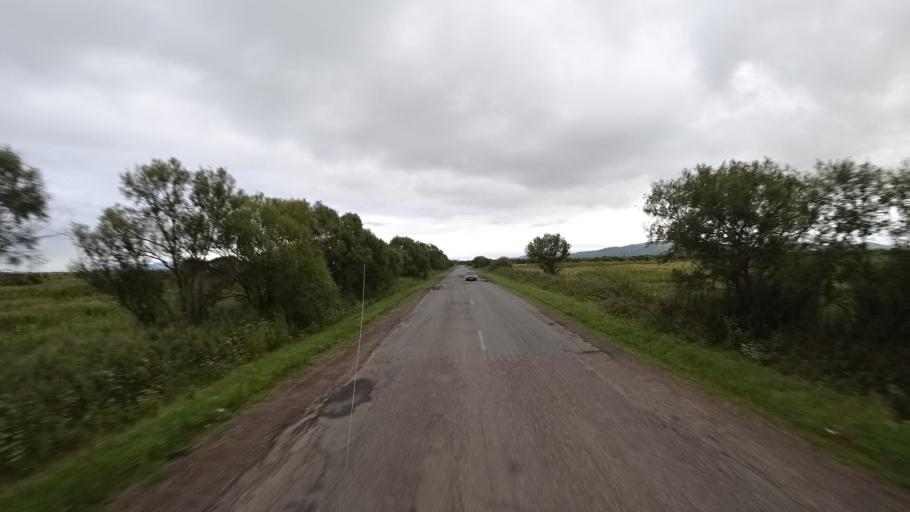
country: RU
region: Primorskiy
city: Chernigovka
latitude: 44.3603
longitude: 132.5563
